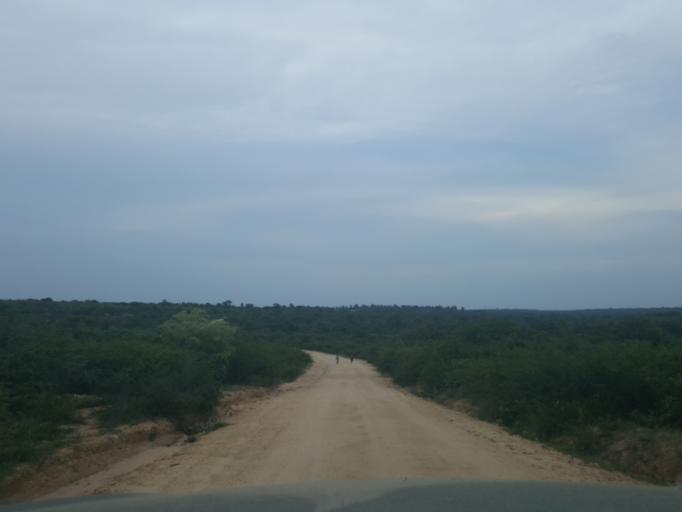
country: ZA
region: Limpopo
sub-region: Mopani District Municipality
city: Hoedspruit
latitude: -24.5766
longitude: 30.9945
